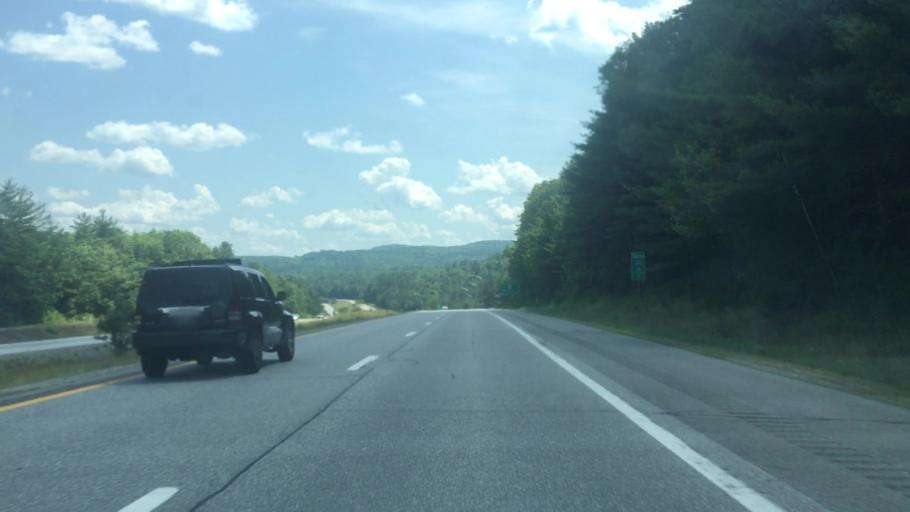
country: US
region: New Hampshire
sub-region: Merrimack County
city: Henniker
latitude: 43.2950
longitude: -71.8391
